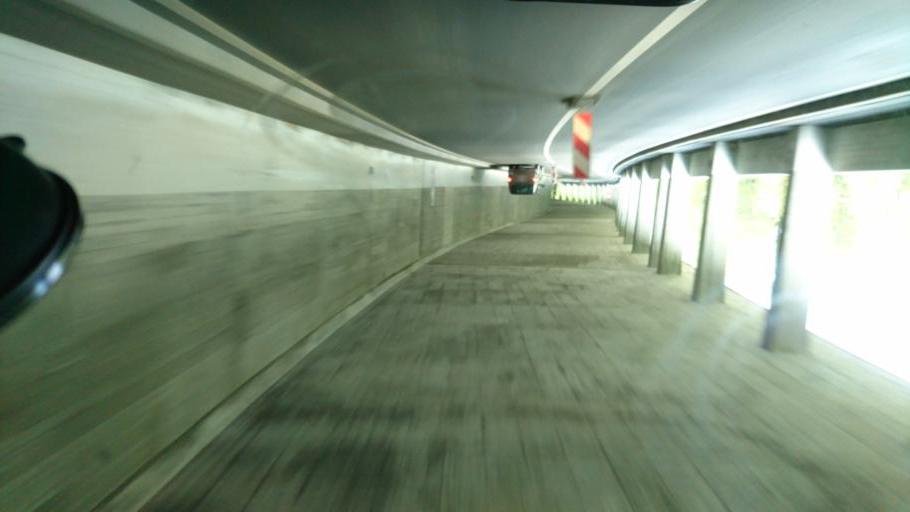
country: CH
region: Valais
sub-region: Brig District
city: Brig
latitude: 46.2718
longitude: 8.0407
